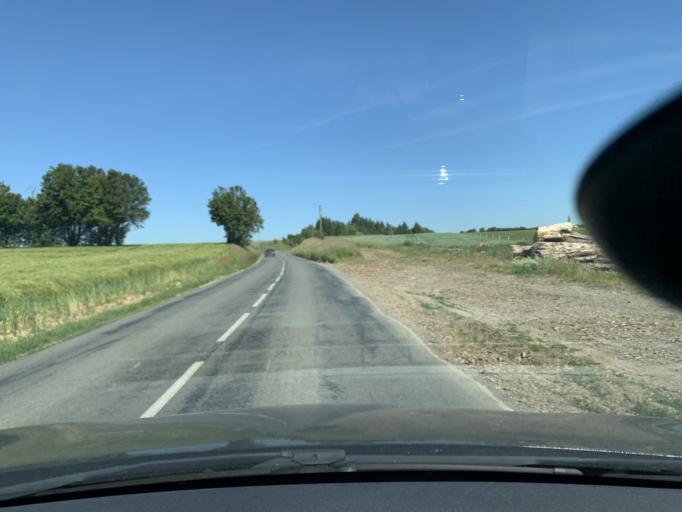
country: FR
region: Nord-Pas-de-Calais
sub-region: Departement du Nord
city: Fontaine-Notre-Dame
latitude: 50.1546
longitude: 3.1640
